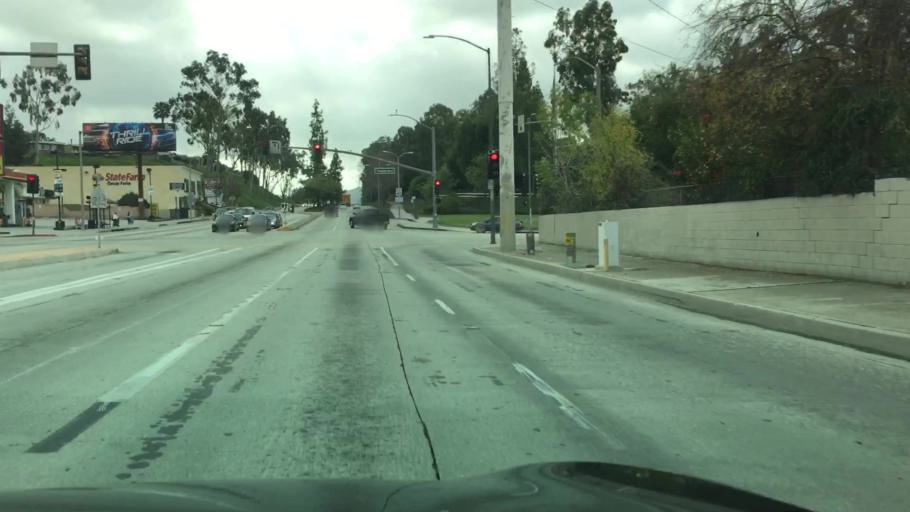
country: US
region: California
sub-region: Los Angeles County
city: South San Jose Hills
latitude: 34.0252
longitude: -117.9176
